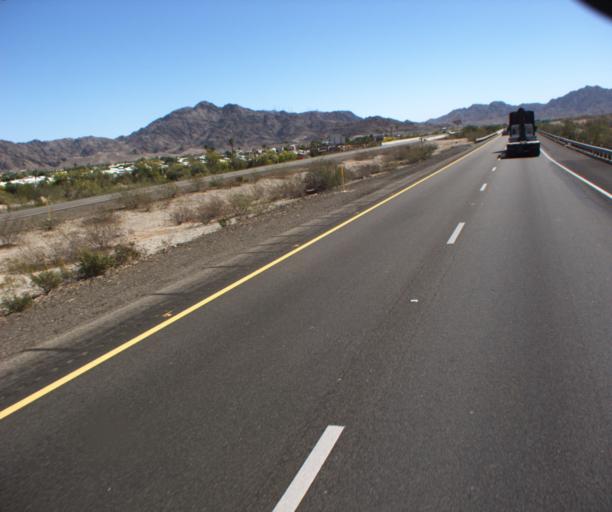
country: US
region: Arizona
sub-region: Yuma County
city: Fortuna Foothills
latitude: 32.6683
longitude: -114.4019
